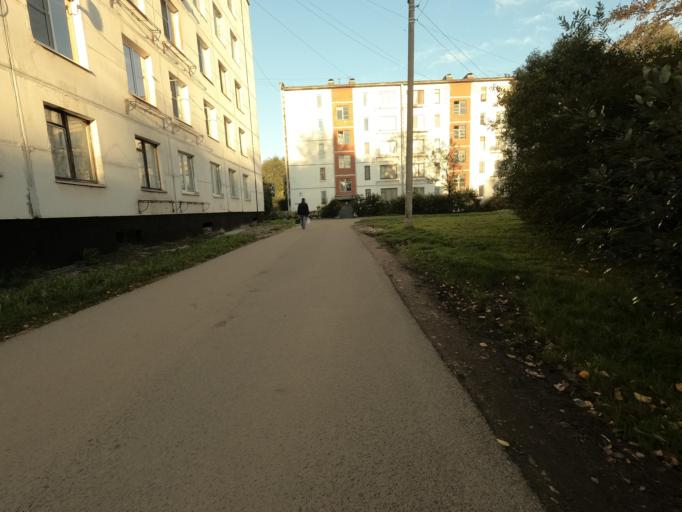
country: RU
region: Leningrad
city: Nikol'skoye
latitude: 59.7051
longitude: 30.7924
